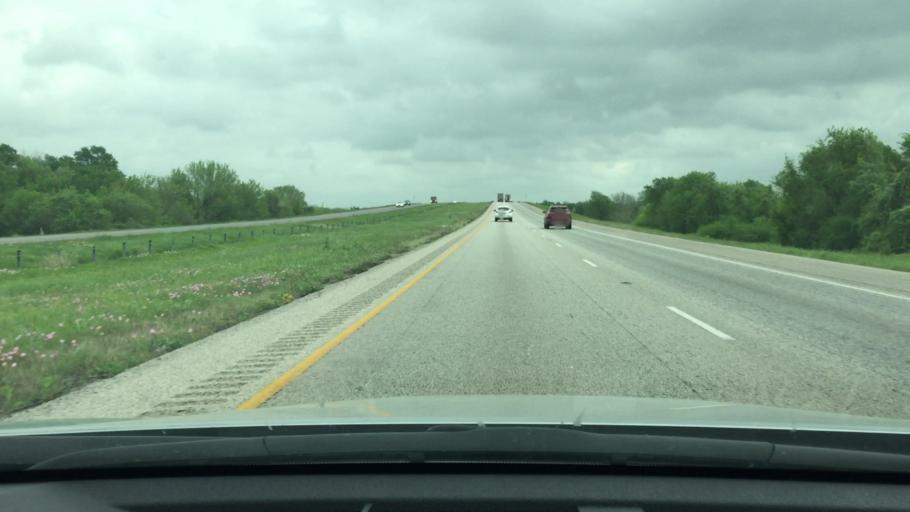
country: US
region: Texas
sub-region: Gonzales County
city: Waelder
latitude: 29.6801
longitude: -97.2732
